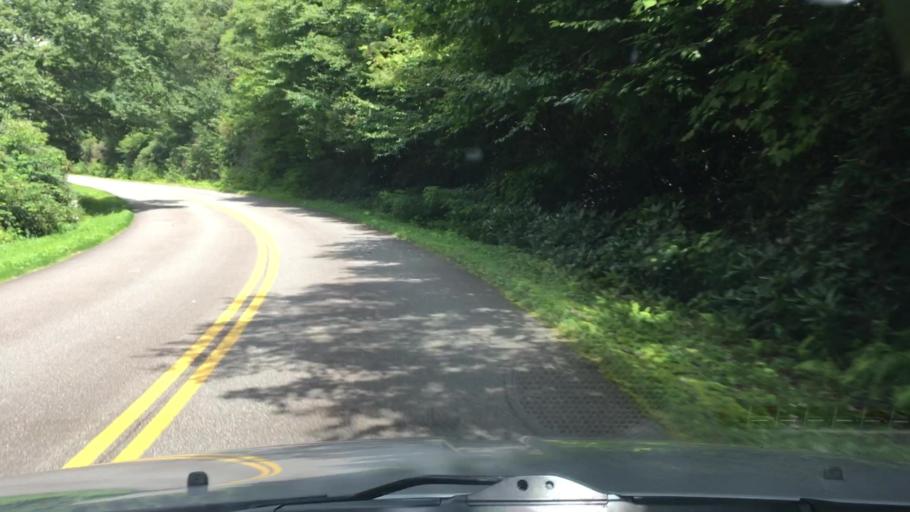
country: US
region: North Carolina
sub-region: Buncombe County
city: Black Mountain
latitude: 35.7010
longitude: -82.2578
